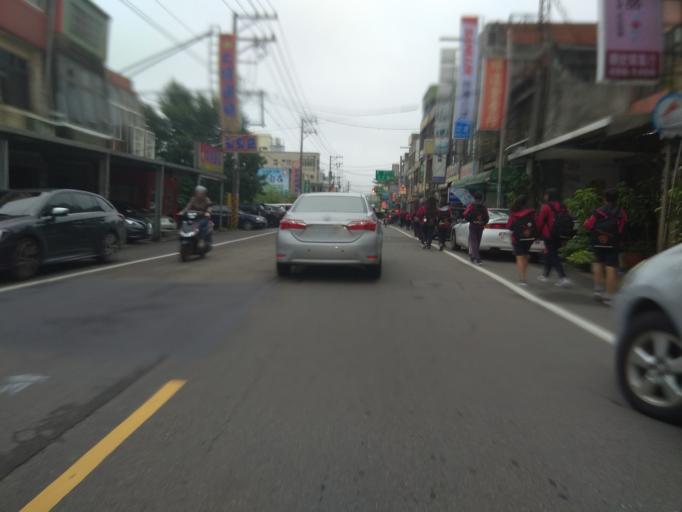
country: TW
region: Taiwan
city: Taoyuan City
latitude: 25.0137
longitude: 121.1345
